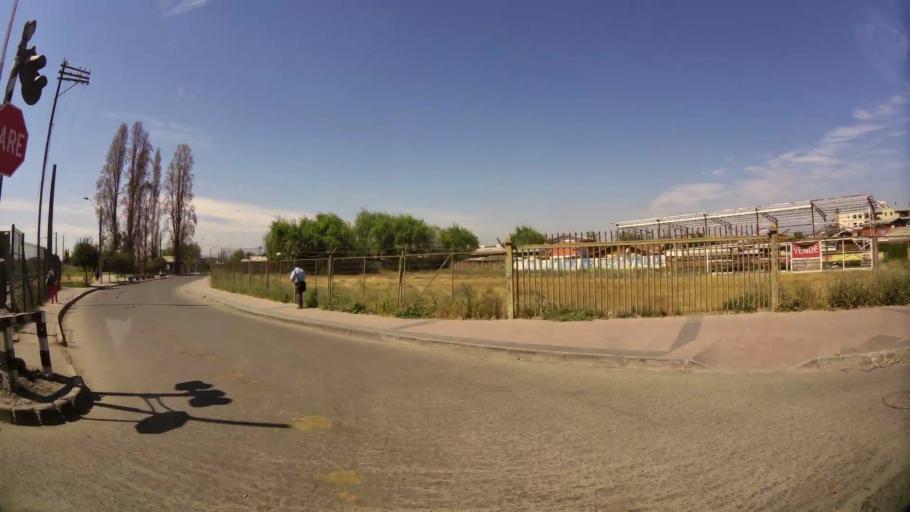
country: CL
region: Santiago Metropolitan
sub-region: Provincia de Talagante
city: Talagante
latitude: -33.6581
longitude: -70.9240
